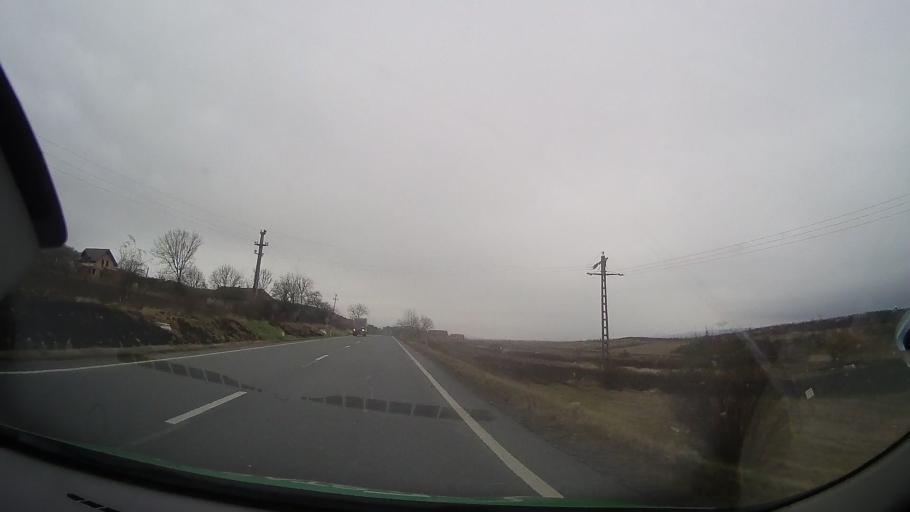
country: RO
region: Mures
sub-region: Comuna Breaza
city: Breaza
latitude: 46.7756
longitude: 24.6564
